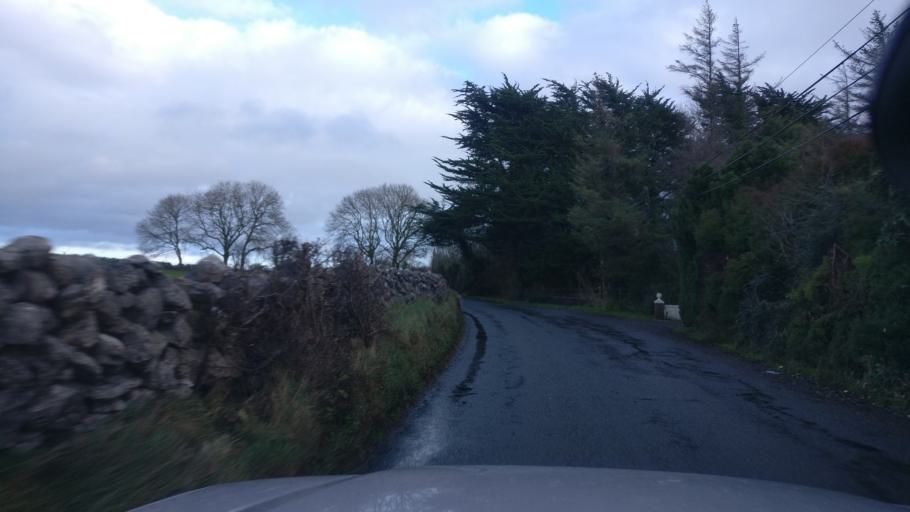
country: IE
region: Connaught
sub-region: County Galway
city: Athenry
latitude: 53.3002
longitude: -8.7279
